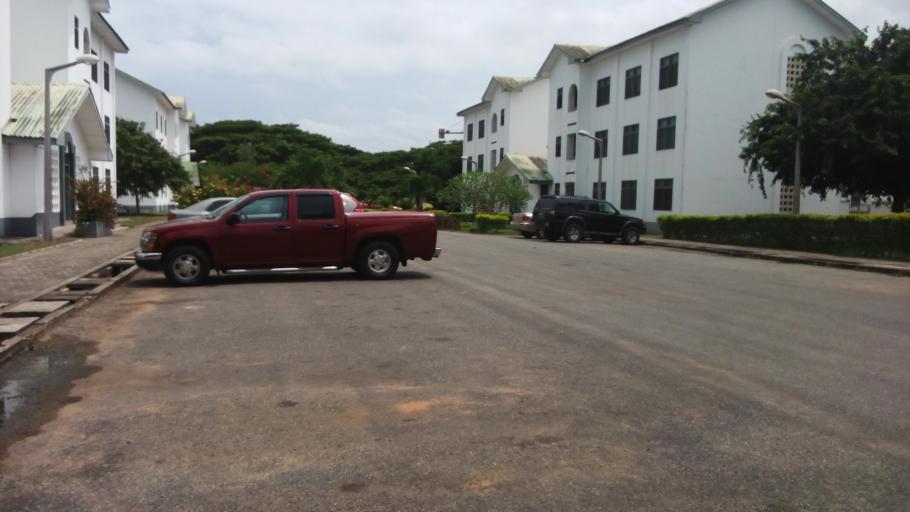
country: GH
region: Central
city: Cape Coast
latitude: 5.1210
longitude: -1.2852
